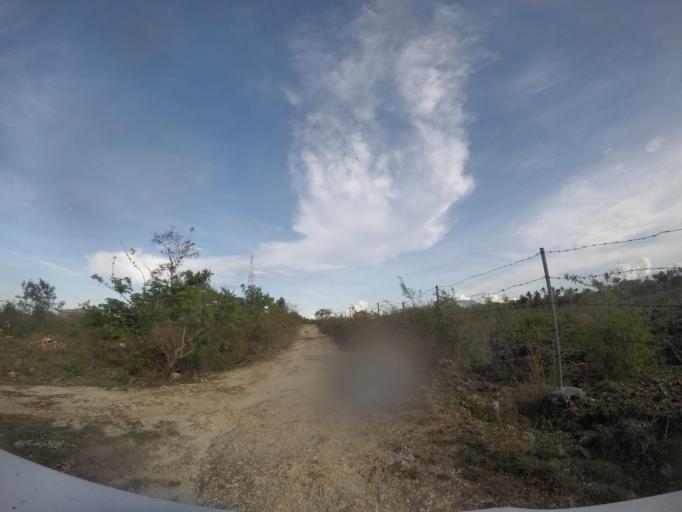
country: TL
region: Baucau
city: Baucau
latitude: -8.4881
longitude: 126.4492
